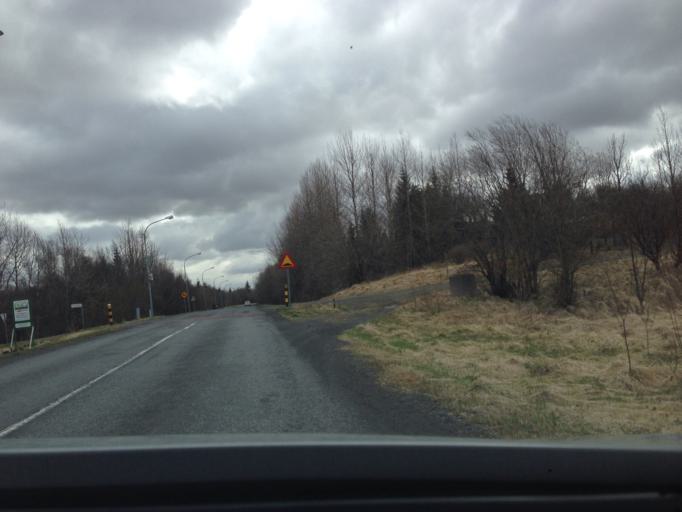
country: IS
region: South
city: Selfoss
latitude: 64.1195
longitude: -20.5026
